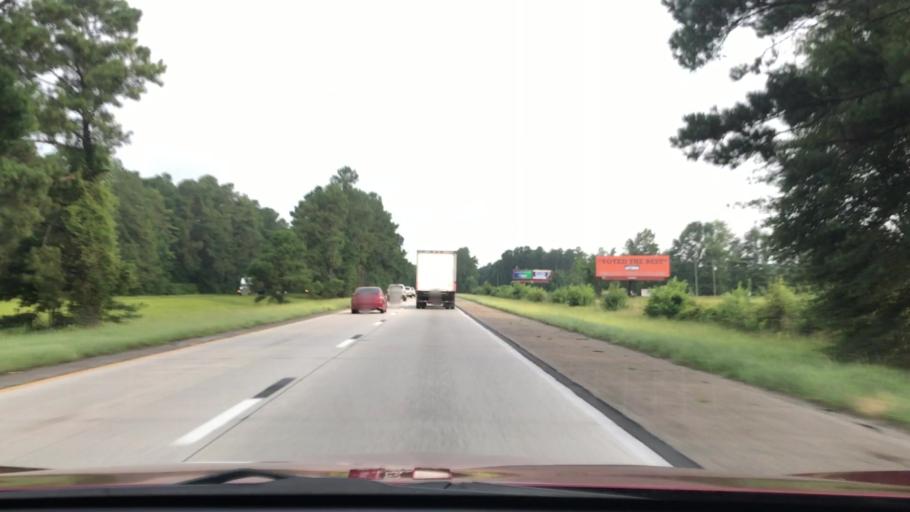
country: US
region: South Carolina
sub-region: Dorchester County
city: Ridgeville
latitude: 33.1893
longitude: -80.3879
